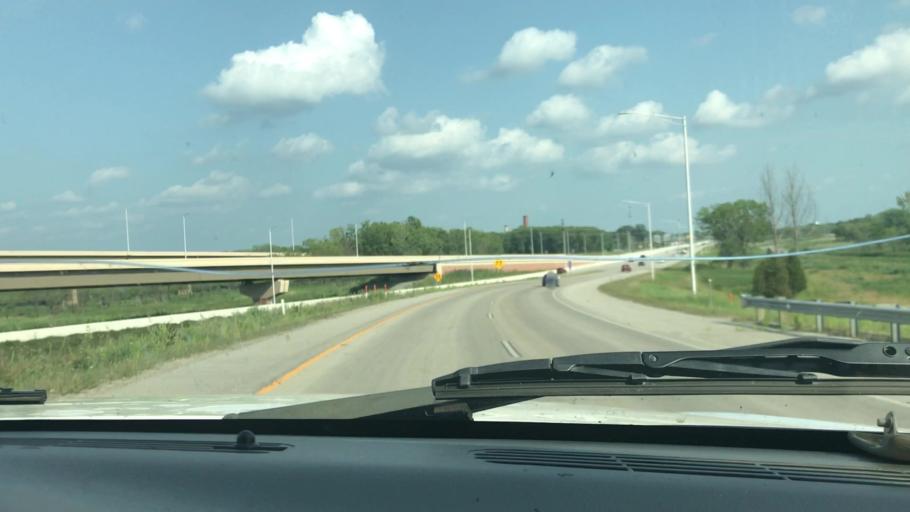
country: US
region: Wisconsin
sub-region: Brown County
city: Howard
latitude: 44.5586
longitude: -88.0515
